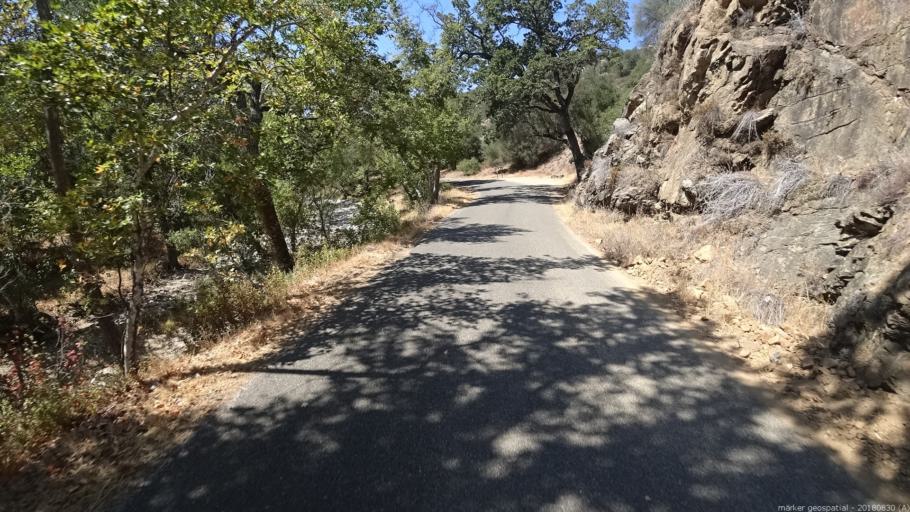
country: US
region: California
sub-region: Monterey County
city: King City
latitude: 35.9901
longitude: -121.3616
